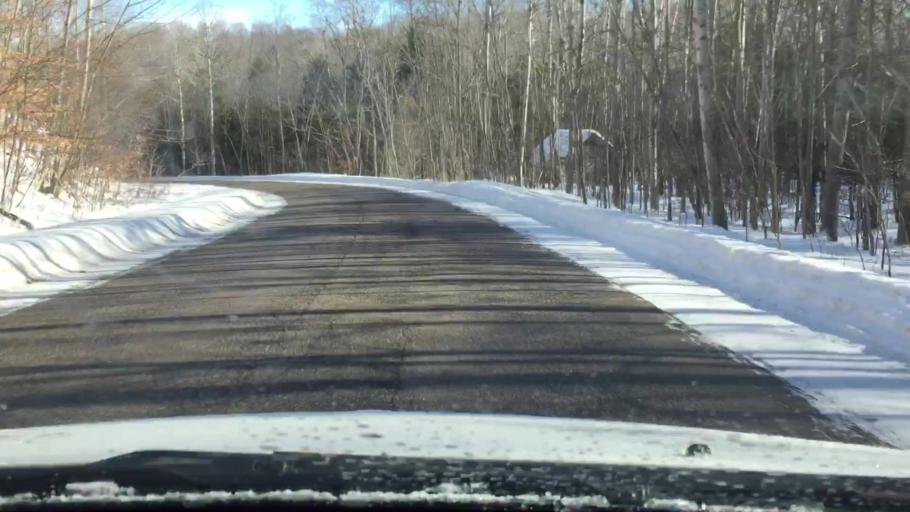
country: US
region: Michigan
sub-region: Charlevoix County
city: East Jordan
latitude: 45.1025
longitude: -85.1413
